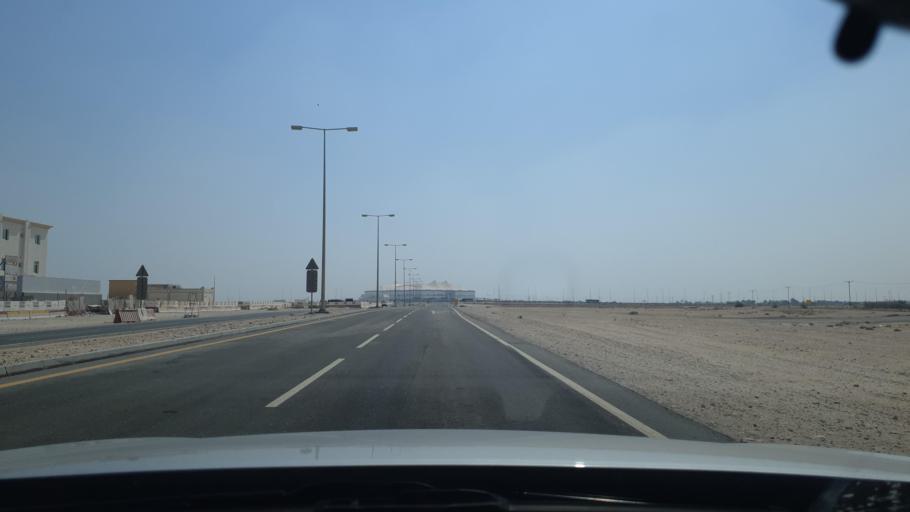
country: QA
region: Al Khawr
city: Al Khawr
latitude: 25.6707
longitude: 51.4716
